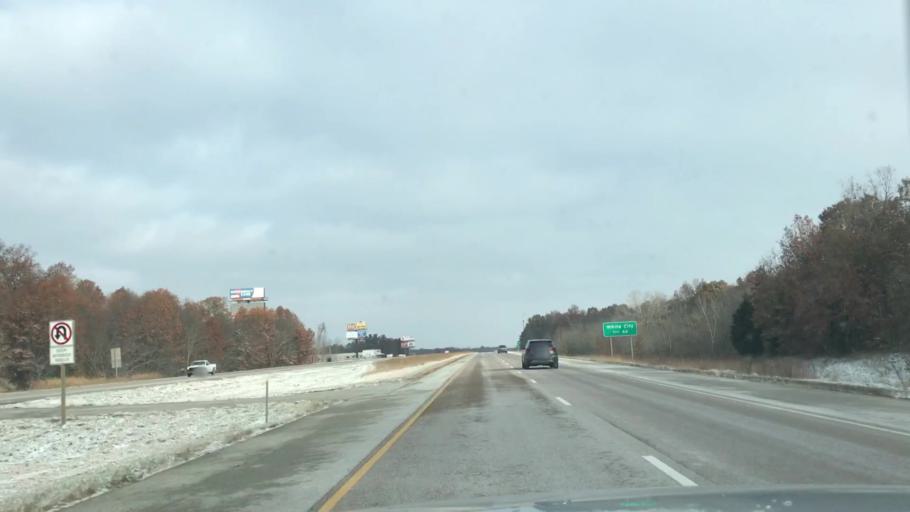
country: US
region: Illinois
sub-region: Macoupin County
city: Mount Olive
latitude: 39.0621
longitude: -89.7556
